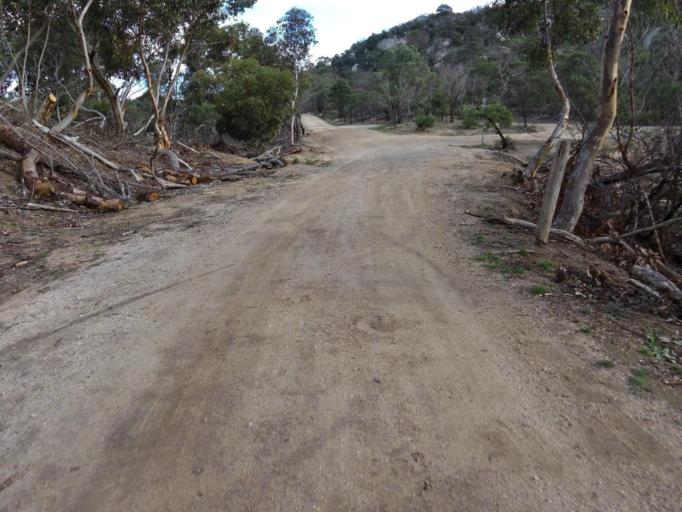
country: AU
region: Victoria
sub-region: Wyndham
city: Little River
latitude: -37.9323
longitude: 144.4423
